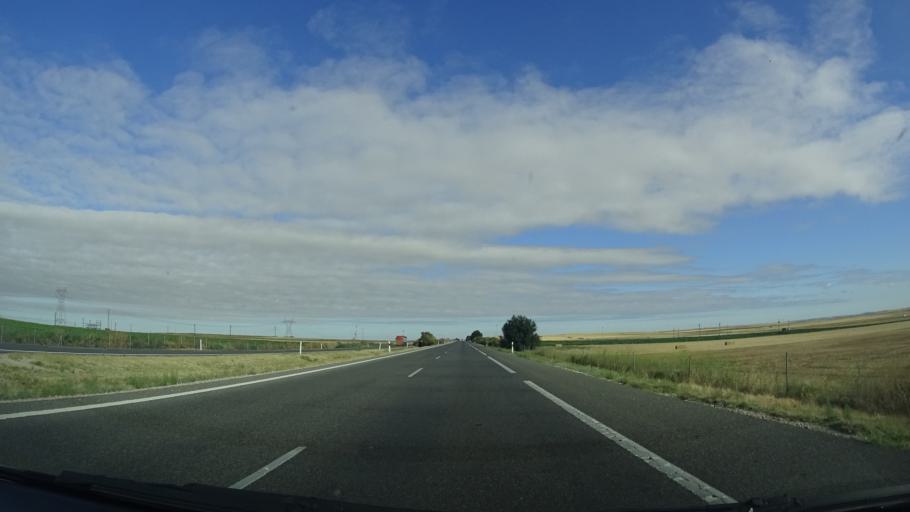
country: ES
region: Castille and Leon
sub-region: Provincia de Valladolid
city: Ataquines
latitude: 41.1941
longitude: -4.8160
